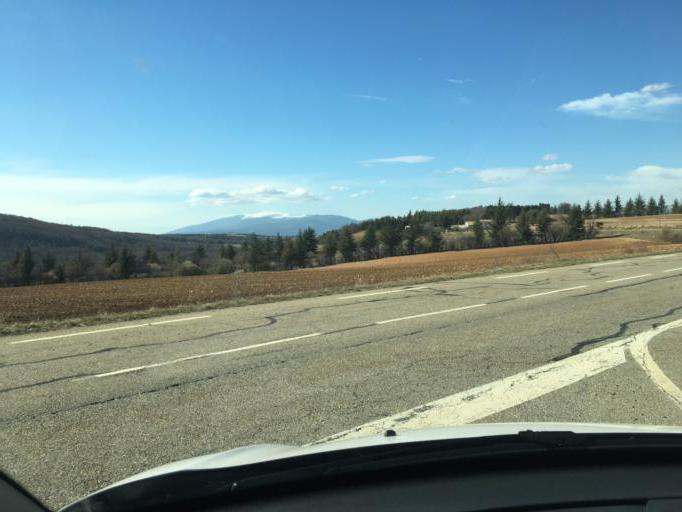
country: FR
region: Provence-Alpes-Cote d'Azur
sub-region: Departement du Vaucluse
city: Sault
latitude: 44.0019
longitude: 5.4838
